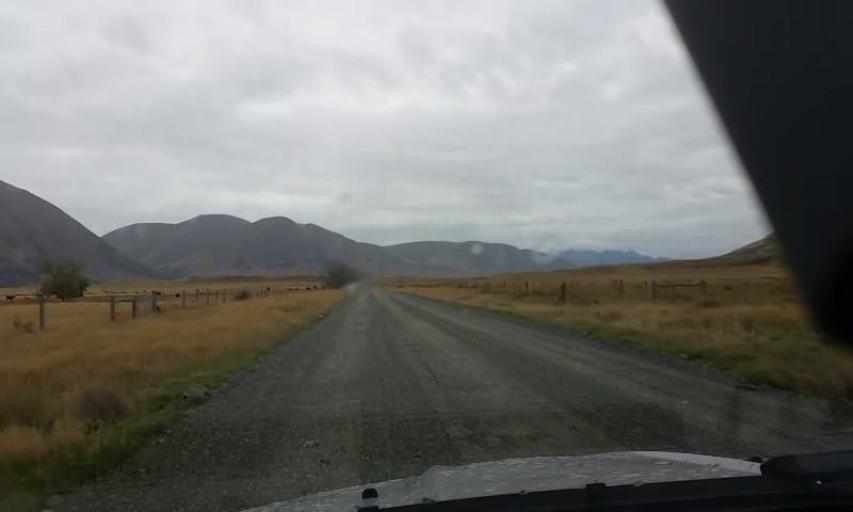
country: NZ
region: Canterbury
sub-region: Ashburton District
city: Methven
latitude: -43.6142
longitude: 171.1166
